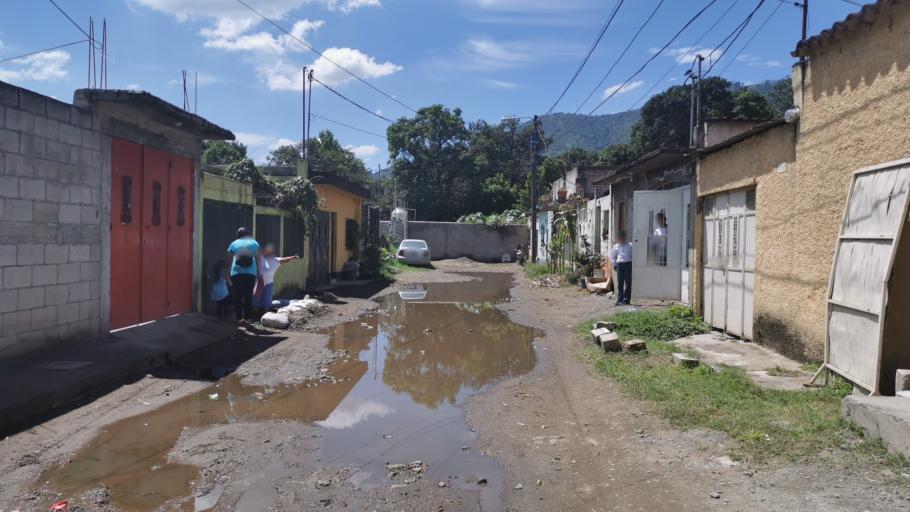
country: GT
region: Guatemala
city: Amatitlan
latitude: 14.4853
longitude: -90.6396
